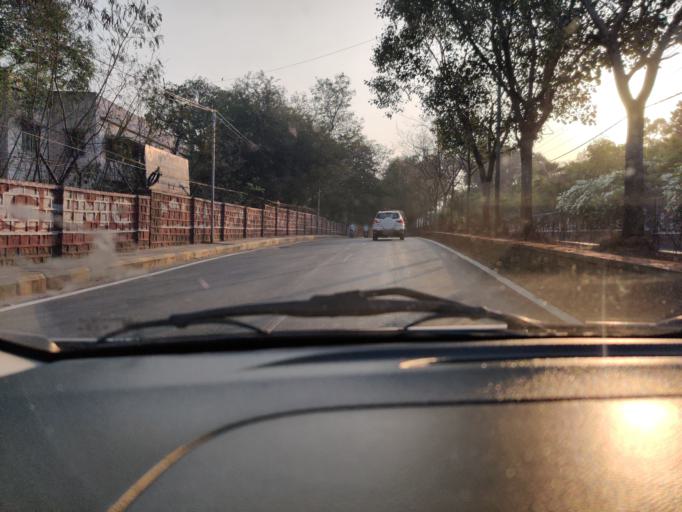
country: IN
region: Telangana
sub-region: Rangareddi
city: Uppal Kalan
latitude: 17.4220
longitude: 78.5448
